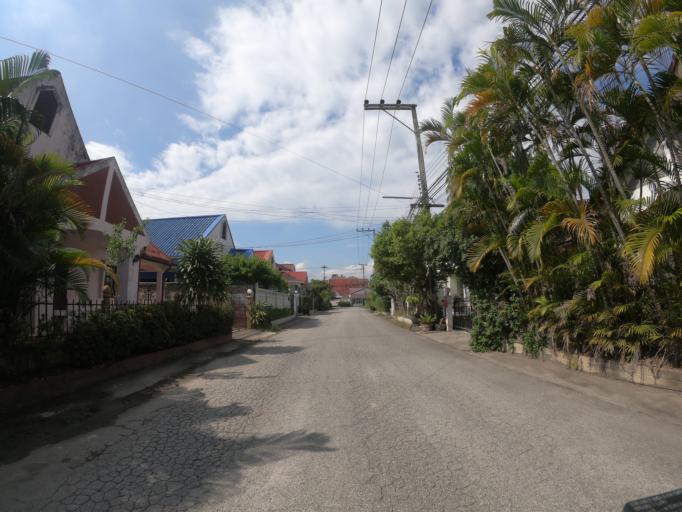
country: TH
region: Chiang Mai
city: Chiang Mai
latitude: 18.7357
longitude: 98.9590
